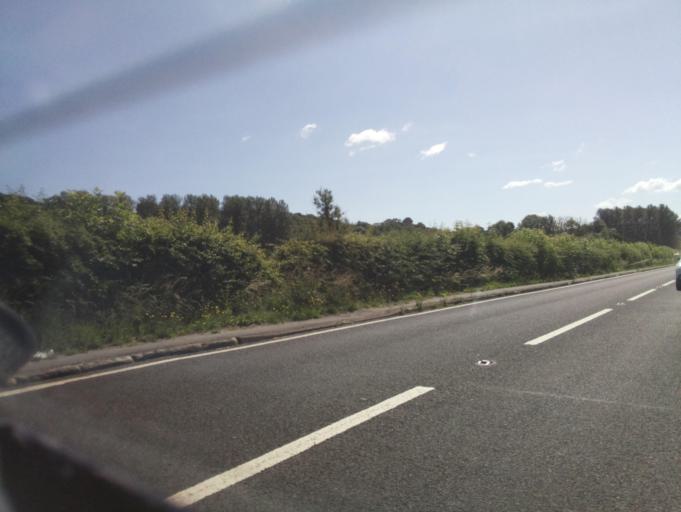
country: GB
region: England
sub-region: Derbyshire
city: Bakewell
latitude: 53.2022
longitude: -1.6637
